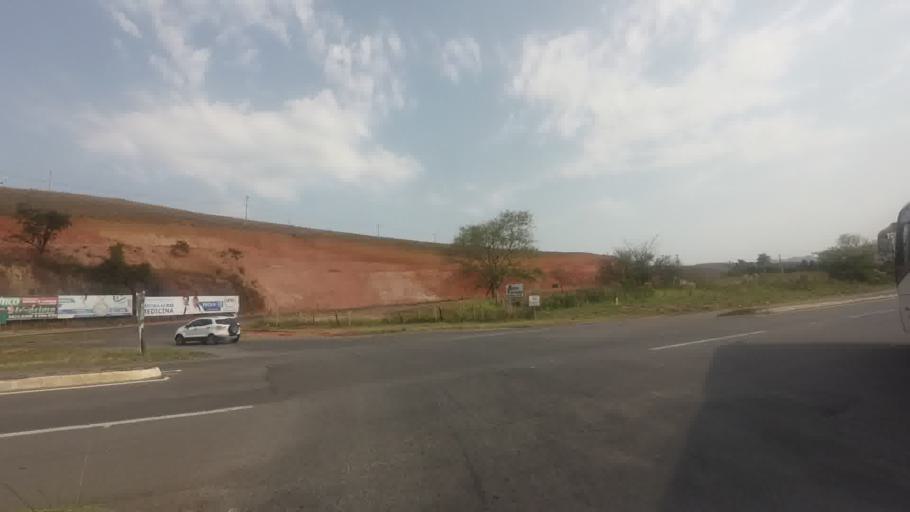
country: BR
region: Rio de Janeiro
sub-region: Itaperuna
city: Itaperuna
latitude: -21.2591
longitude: -41.7699
